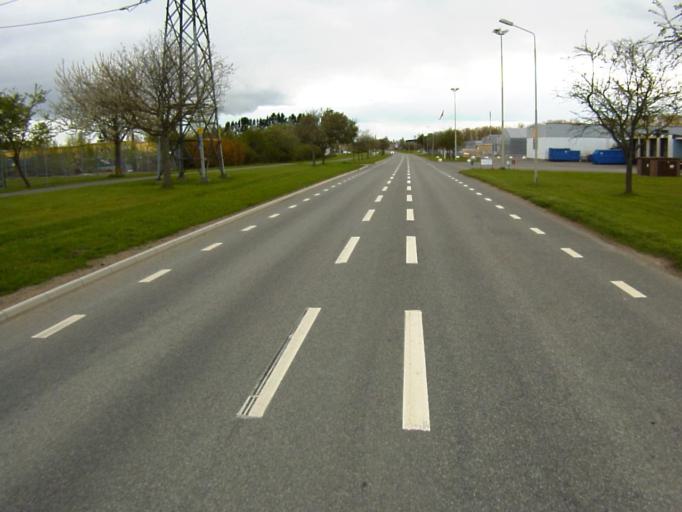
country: SE
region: Skane
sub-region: Kristianstads Kommun
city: Kristianstad
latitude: 56.0566
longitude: 14.1691
